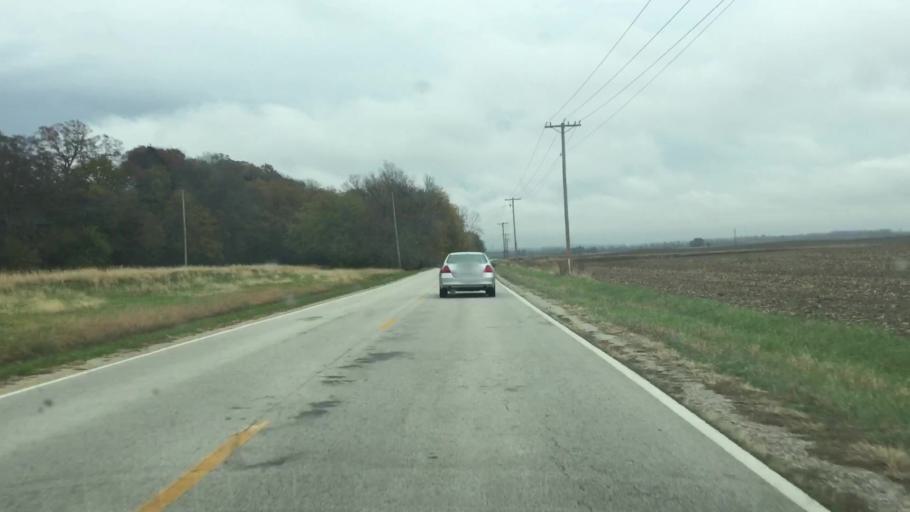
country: US
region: Missouri
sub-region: Gasconade County
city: Hermann
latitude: 38.7239
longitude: -91.4910
